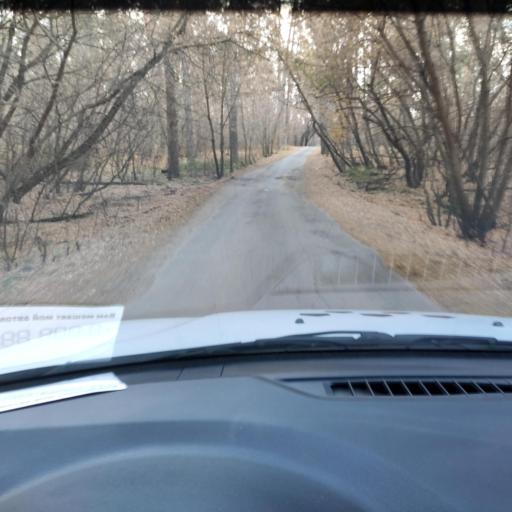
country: RU
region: Samara
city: Tol'yatti
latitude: 53.5057
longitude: 49.3855
